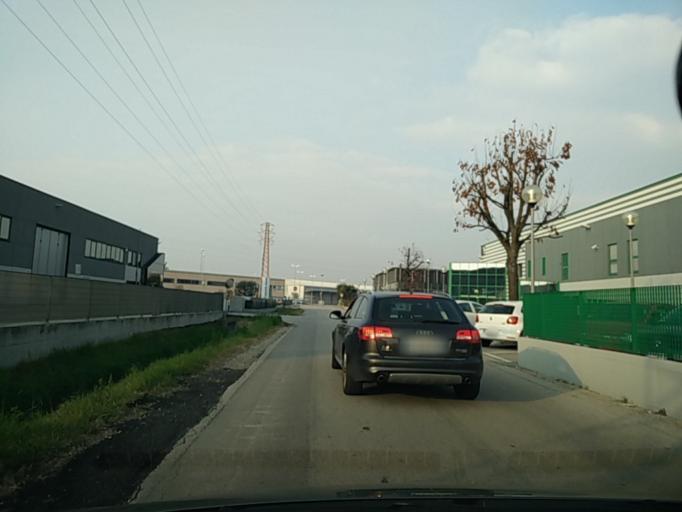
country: IT
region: Veneto
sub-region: Provincia di Treviso
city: Salvatronda
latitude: 45.6791
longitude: 11.9643
